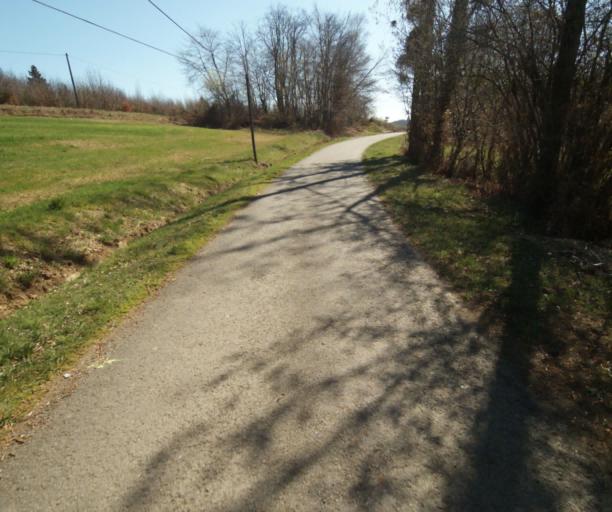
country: FR
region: Limousin
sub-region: Departement de la Correze
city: Saint-Mexant
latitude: 45.2999
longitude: 1.6718
